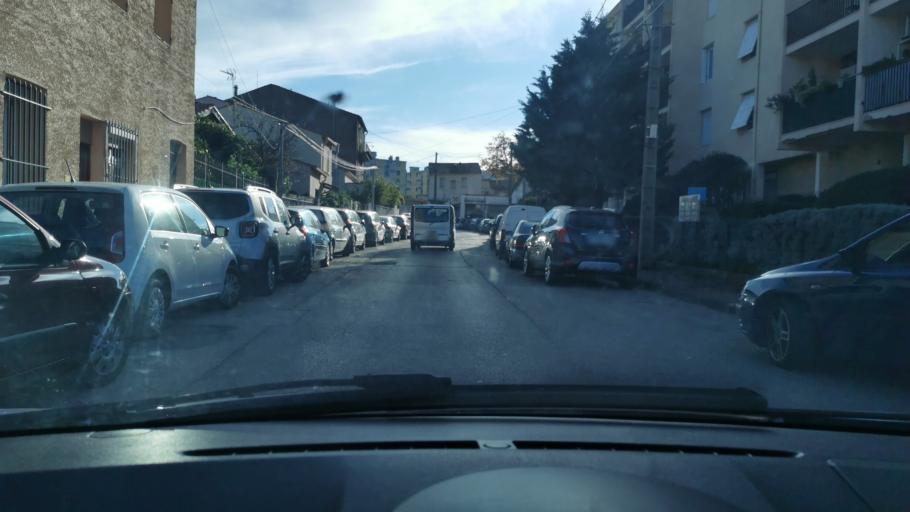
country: FR
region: Languedoc-Roussillon
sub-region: Departement de l'Herault
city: Sete
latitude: 43.4113
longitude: 3.6764
